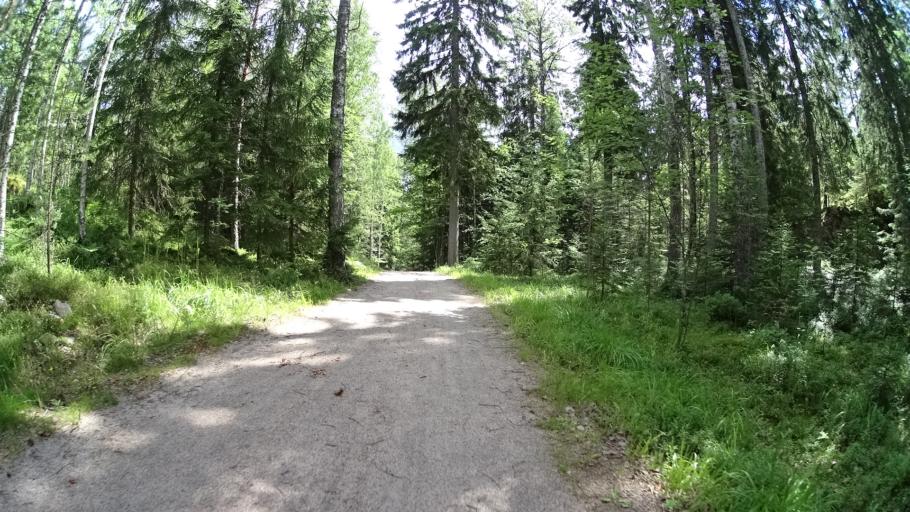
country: FI
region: Uusimaa
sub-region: Helsinki
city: Espoo
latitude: 60.2835
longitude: 24.6036
